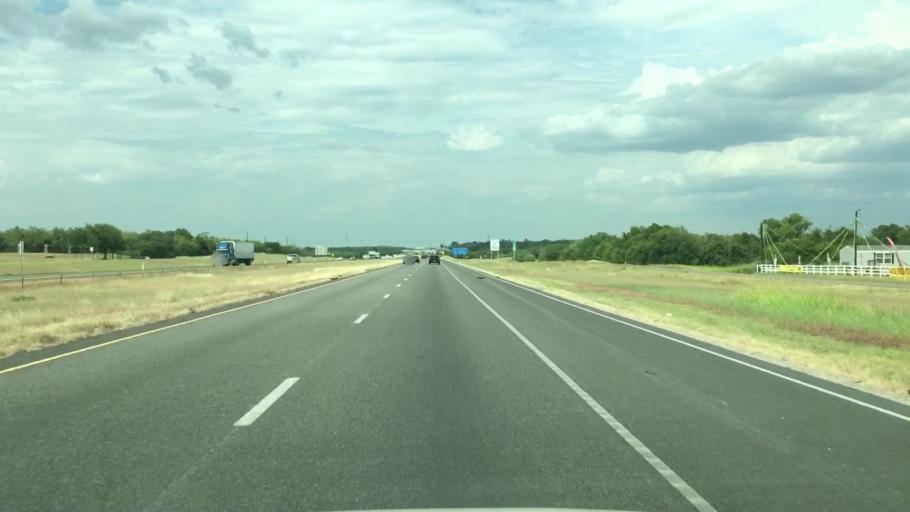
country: US
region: Texas
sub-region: Bexar County
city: Elmendorf
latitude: 29.2246
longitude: -98.4089
